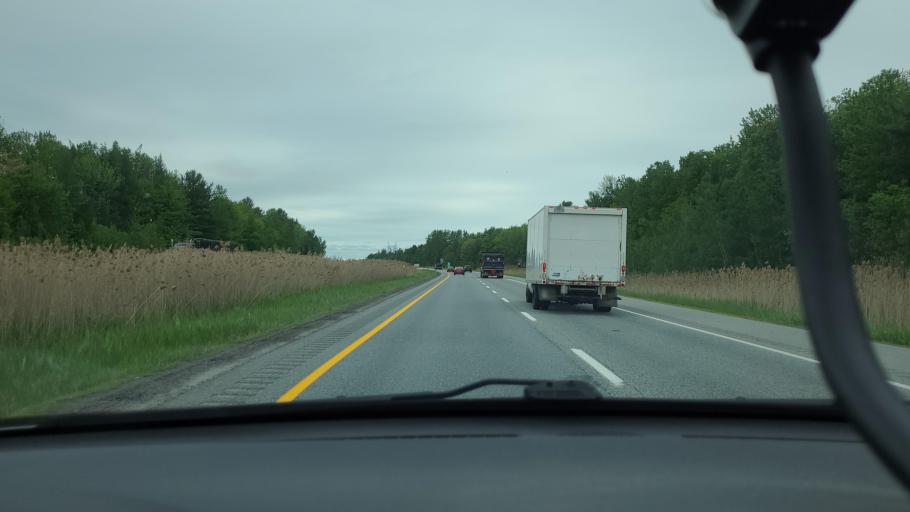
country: CA
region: Quebec
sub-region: Lanaudiere
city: Mascouche
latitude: 45.8106
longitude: -73.5930
